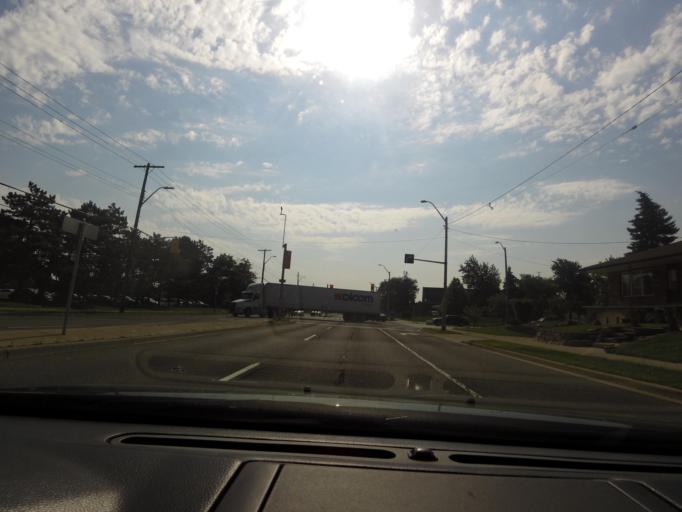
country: CA
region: Ontario
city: Hamilton
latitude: 43.2233
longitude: -79.8602
